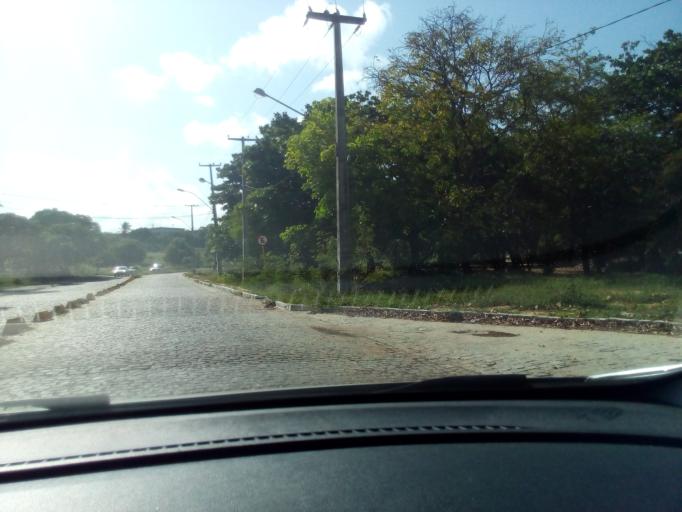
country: BR
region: Rio Grande do Norte
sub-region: Natal
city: Natal
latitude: -5.8386
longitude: -35.2016
